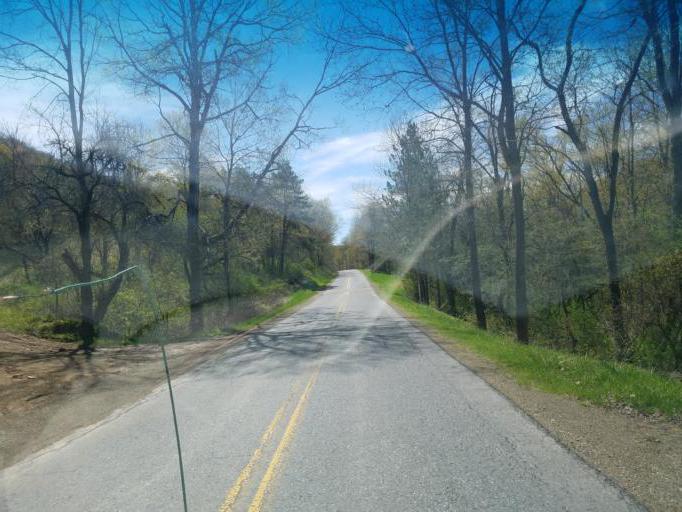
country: US
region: Pennsylvania
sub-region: Potter County
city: Galeton
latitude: 41.8637
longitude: -77.7166
